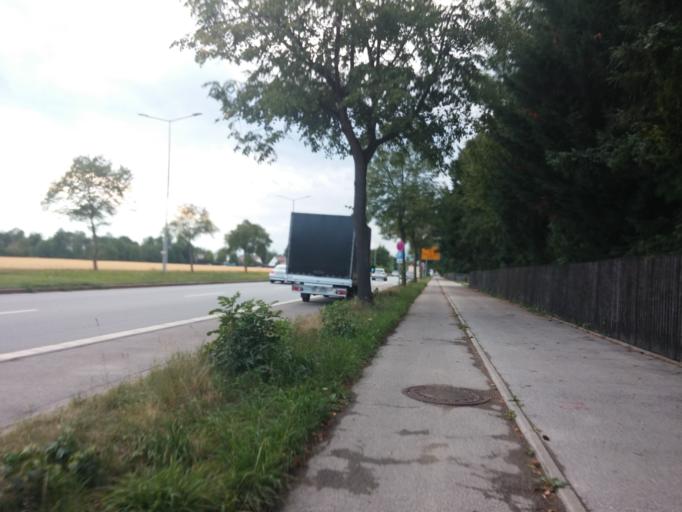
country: DE
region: Bavaria
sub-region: Upper Bavaria
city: Haar
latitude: 48.1052
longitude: 11.7413
